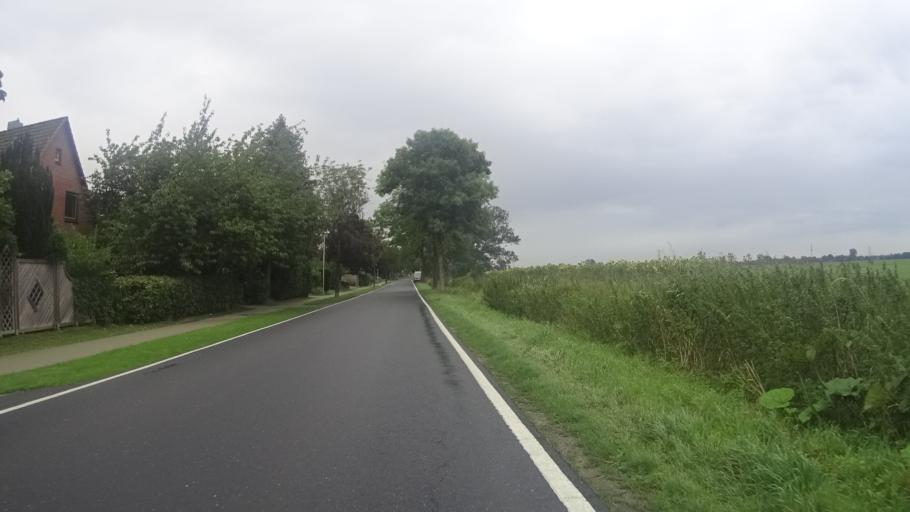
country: DE
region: Schleswig-Holstein
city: Altenmoor
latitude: 53.7838
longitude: 9.5627
